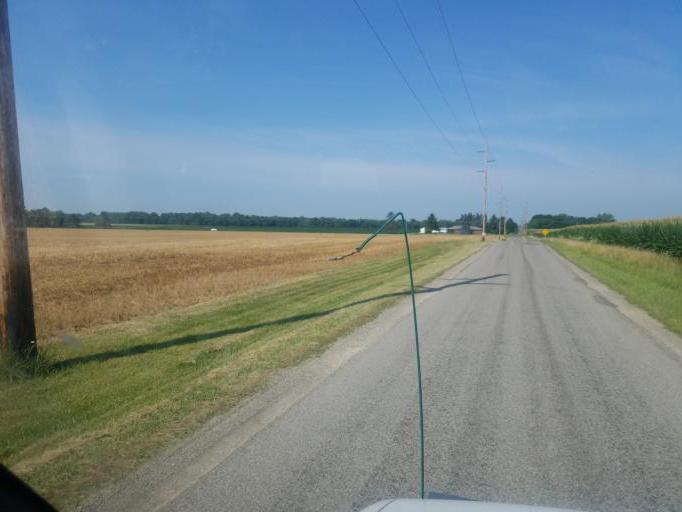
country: US
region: Ohio
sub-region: Union County
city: Marysville
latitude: 40.2873
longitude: -83.3743
